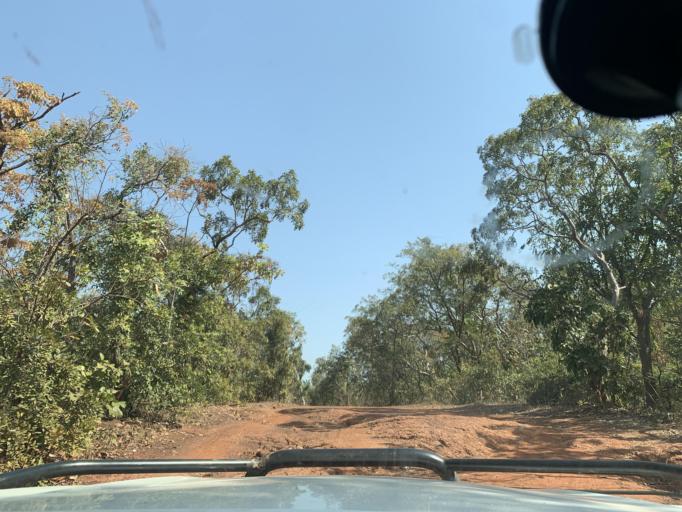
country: ML
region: Sikasso
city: Kolondieba
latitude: 10.8954
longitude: -6.7448
